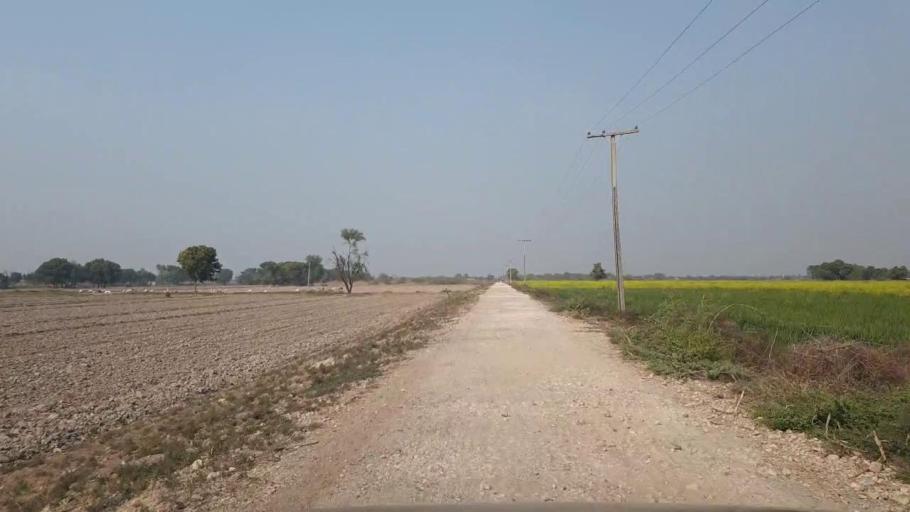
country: PK
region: Sindh
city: Mirwah Gorchani
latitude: 25.3769
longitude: 68.9475
